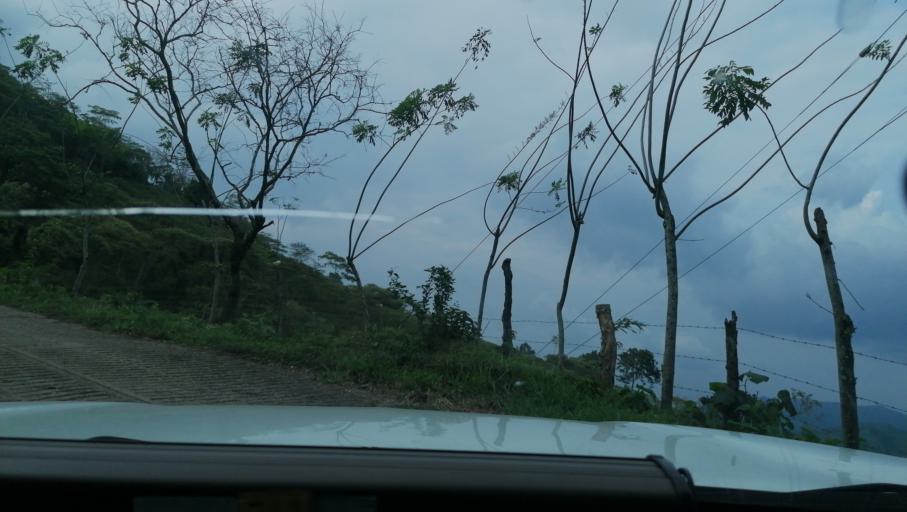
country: MX
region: Chiapas
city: Ixtacomitan
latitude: 17.3348
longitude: -93.1081
